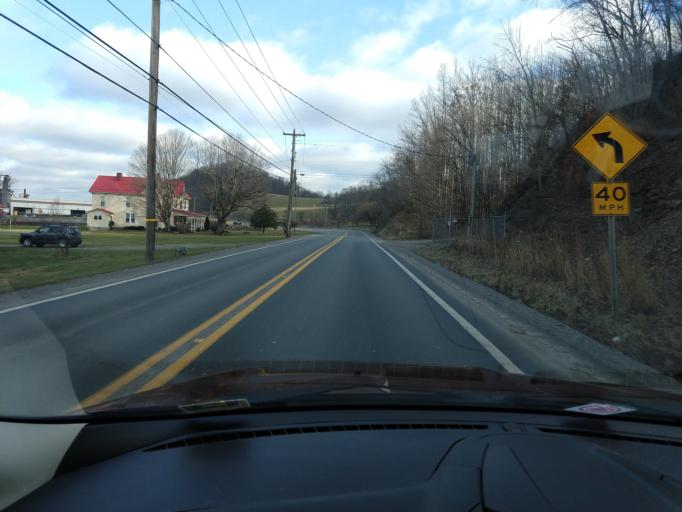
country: US
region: West Virginia
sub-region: Randolph County
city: Elkins
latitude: 38.8128
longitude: -79.8793
